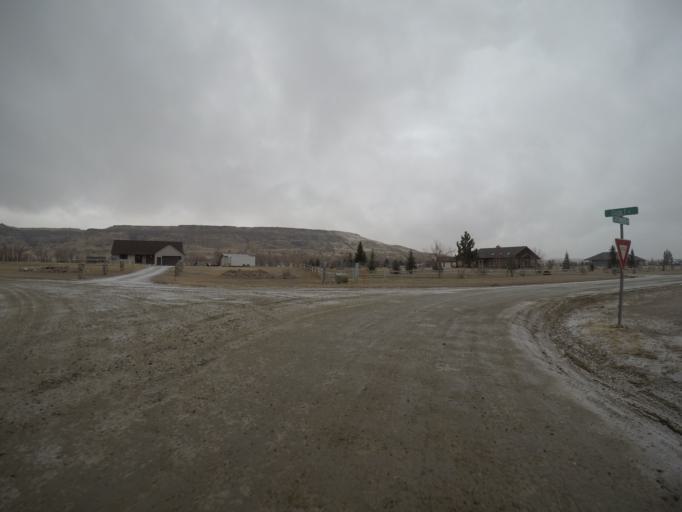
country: US
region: Montana
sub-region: Stillwater County
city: Absarokee
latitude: 45.5294
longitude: -109.4524
